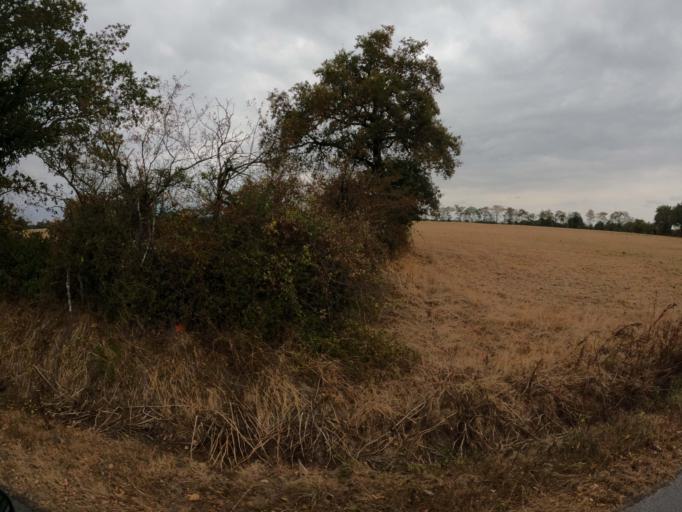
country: FR
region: Pays de la Loire
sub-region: Departement de la Vendee
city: La Boissiere-de-Montaigu
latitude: 46.9765
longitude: -1.1792
